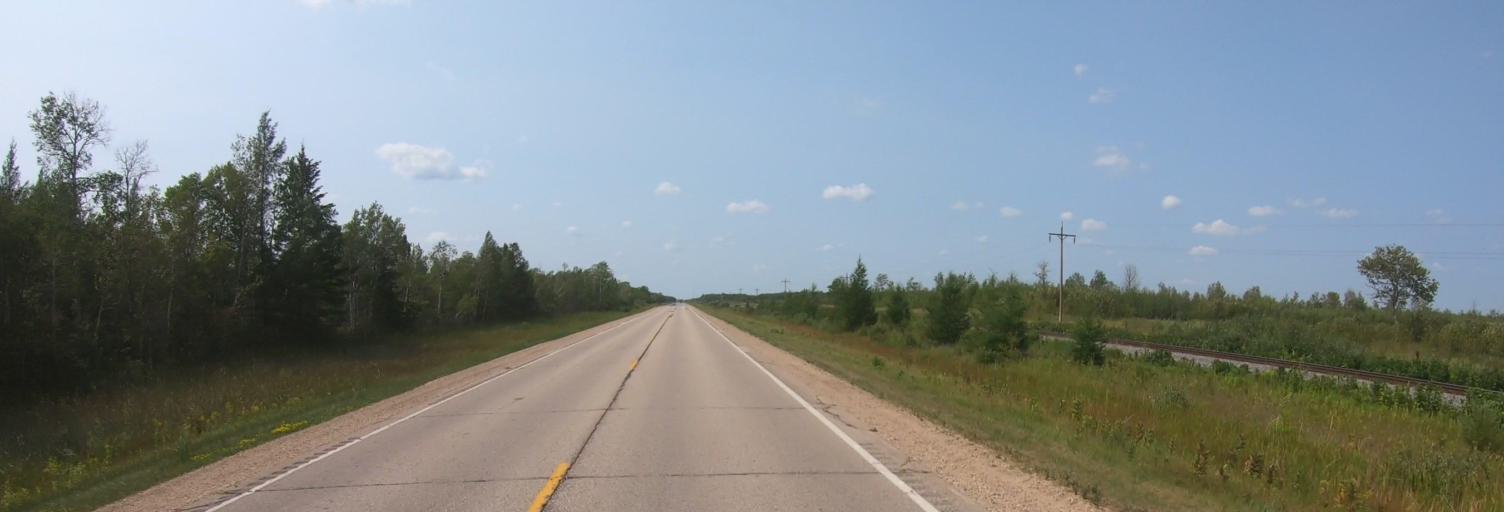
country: US
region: Minnesota
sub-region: Lake of the Woods County
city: Baudette
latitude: 48.7510
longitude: -94.8838
